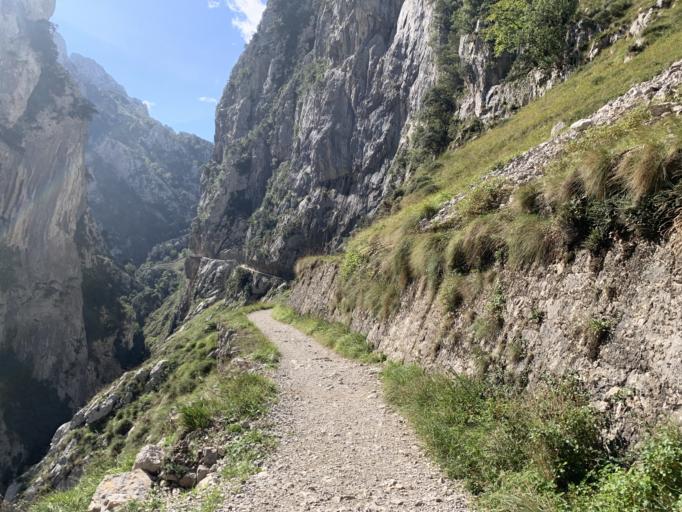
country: ES
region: Asturias
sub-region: Province of Asturias
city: Carrena
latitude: 43.2405
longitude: -4.8904
